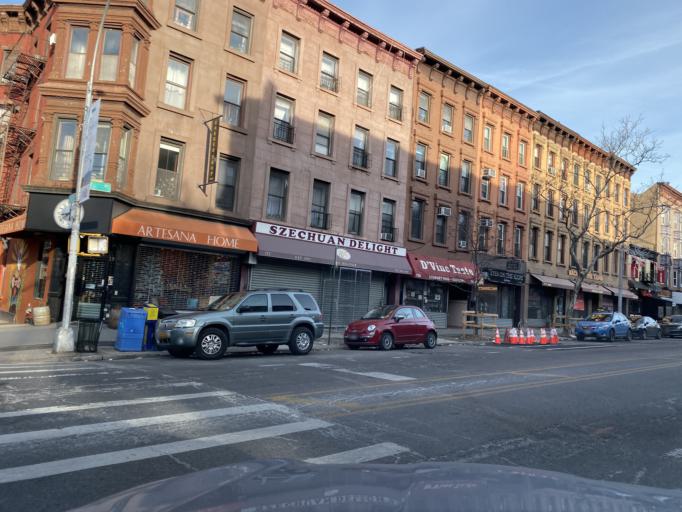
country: US
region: New York
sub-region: Kings County
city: Brooklyn
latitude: 40.6723
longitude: -73.9770
